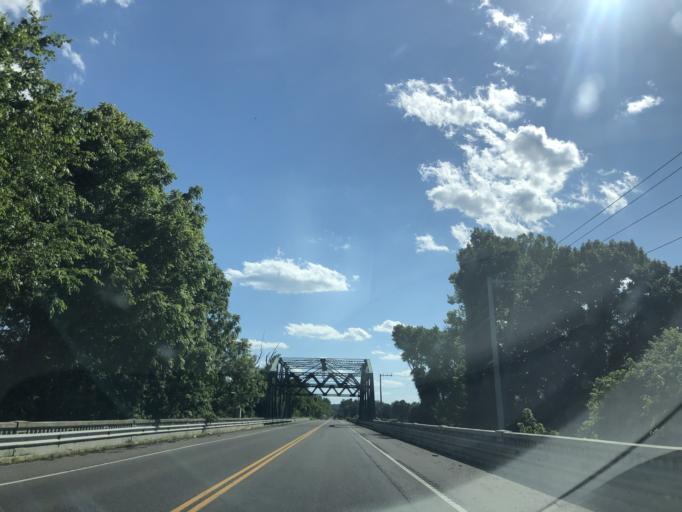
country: US
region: Tennessee
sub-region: Davidson County
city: Belle Meade
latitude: 36.0550
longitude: -86.9279
